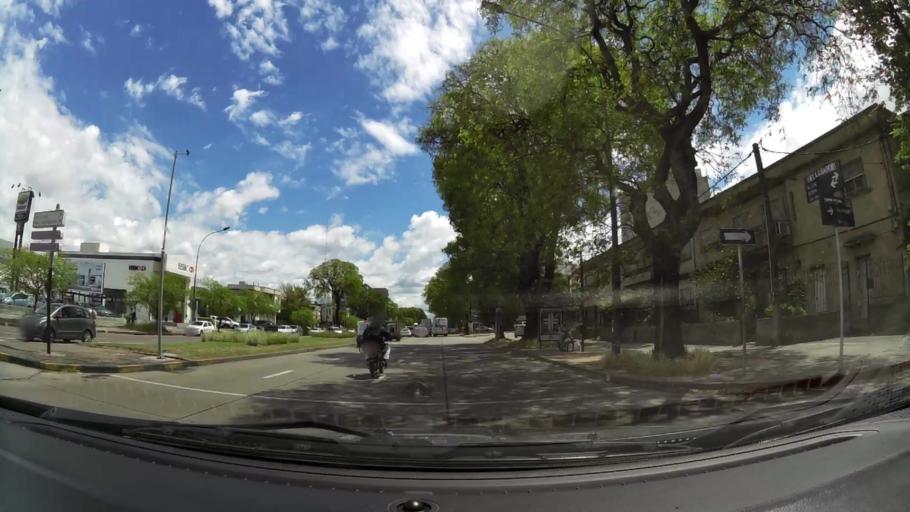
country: UY
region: Montevideo
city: Montevideo
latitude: -34.8896
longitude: -56.1654
